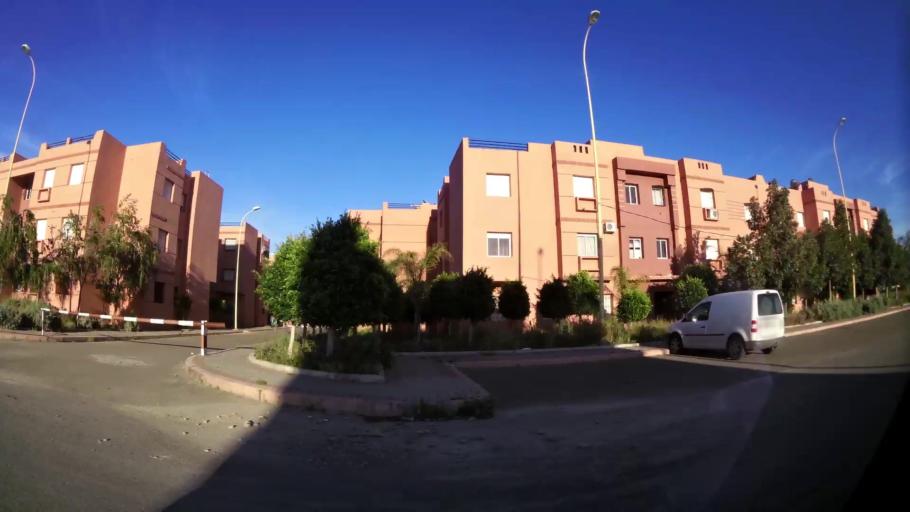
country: MA
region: Marrakech-Tensift-Al Haouz
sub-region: Marrakech
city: Marrakesh
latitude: 31.7503
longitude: -8.1290
